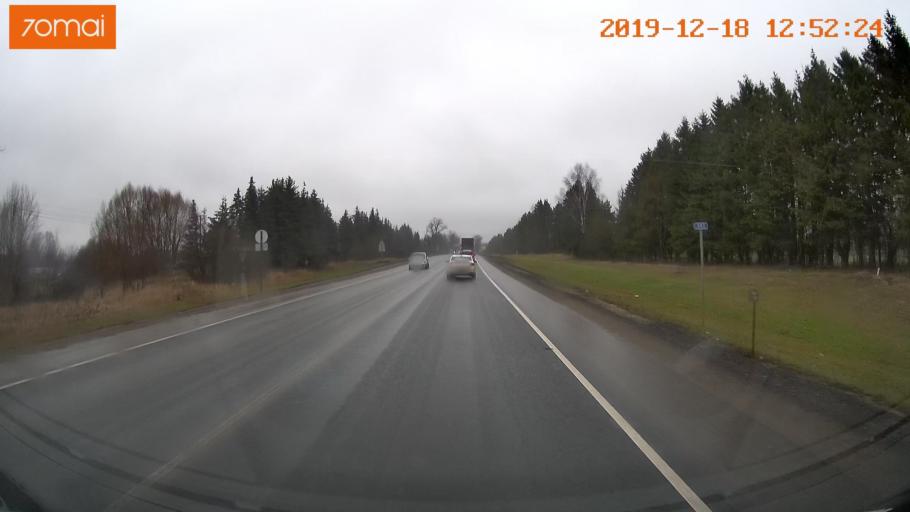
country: RU
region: Moskovskaya
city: Klin
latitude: 56.3111
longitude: 36.6874
